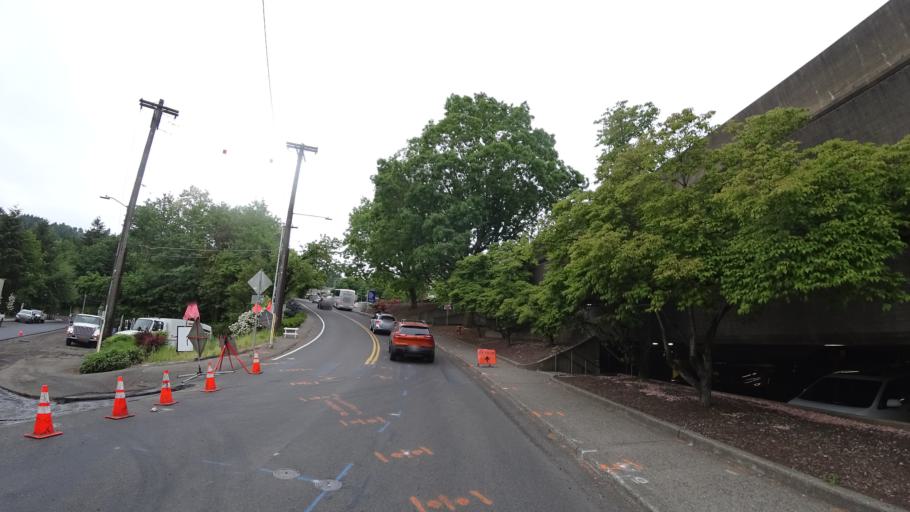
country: US
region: Oregon
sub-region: Multnomah County
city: Portland
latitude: 45.4992
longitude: -122.6881
